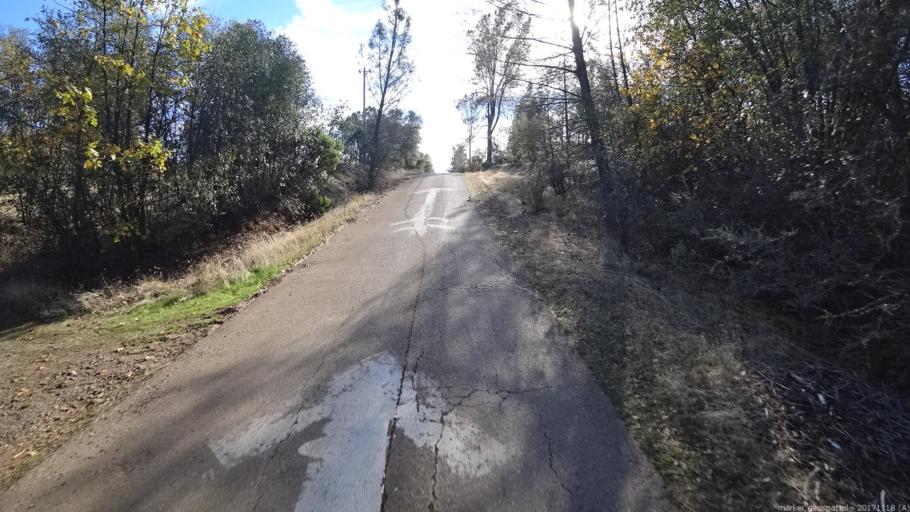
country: US
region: California
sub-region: Shasta County
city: Redding
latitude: 40.4667
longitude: -122.4356
